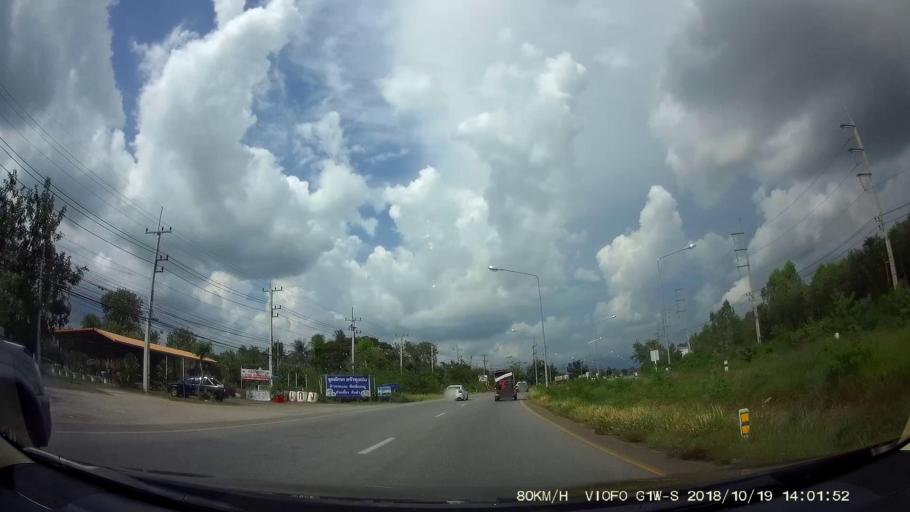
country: TH
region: Chaiyaphum
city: Chaiyaphum
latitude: 15.8344
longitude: 102.0583
